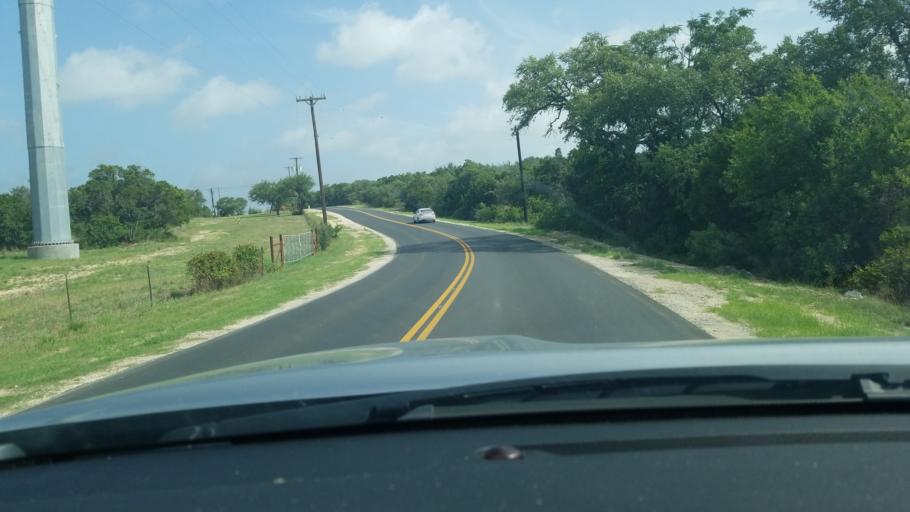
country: US
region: Texas
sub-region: Bexar County
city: Timberwood Park
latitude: 29.7008
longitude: -98.4543
